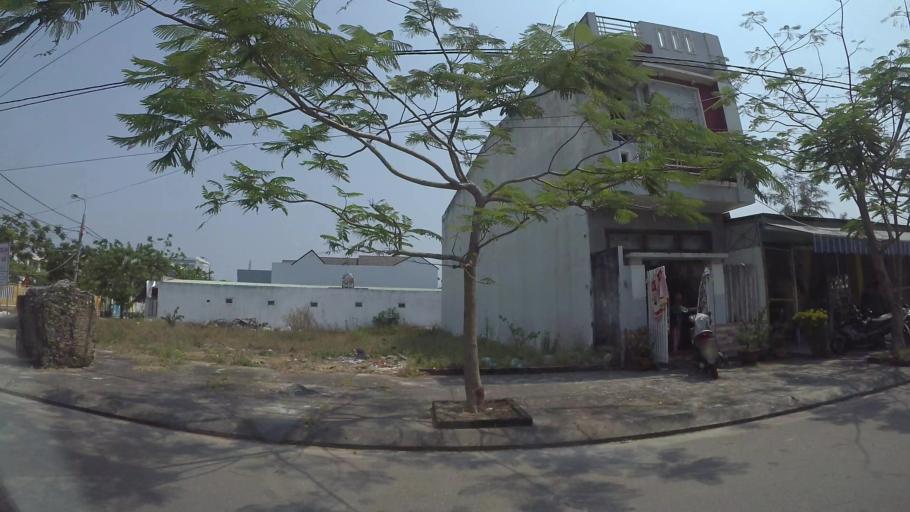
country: VN
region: Da Nang
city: Ngu Hanh Son
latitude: 16.0132
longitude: 108.2515
